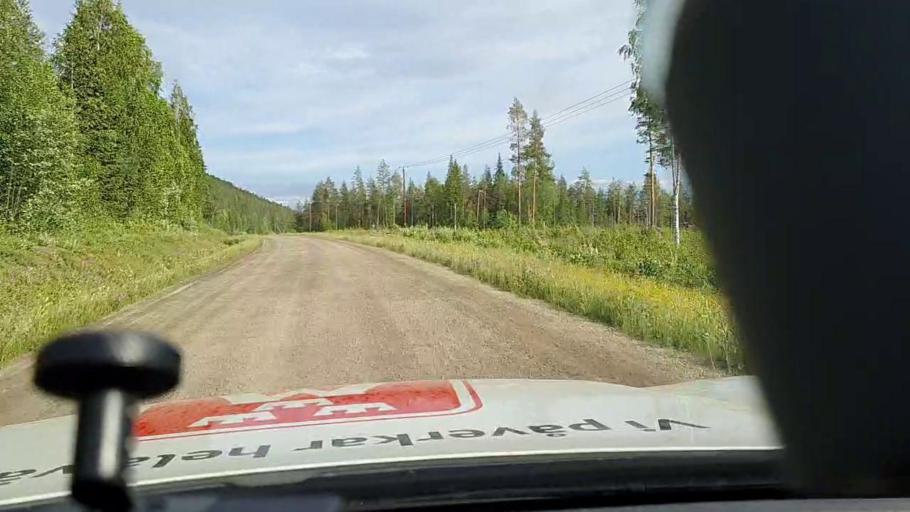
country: SE
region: Norrbotten
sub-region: Alvsbyns Kommun
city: AElvsbyn
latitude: 66.1820
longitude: 21.2208
